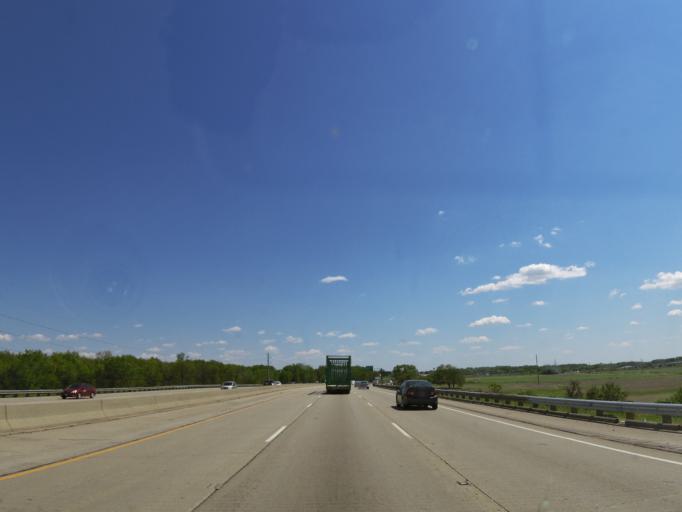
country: US
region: Wisconsin
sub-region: Dane County
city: McFarland
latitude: 43.0659
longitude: -89.2779
